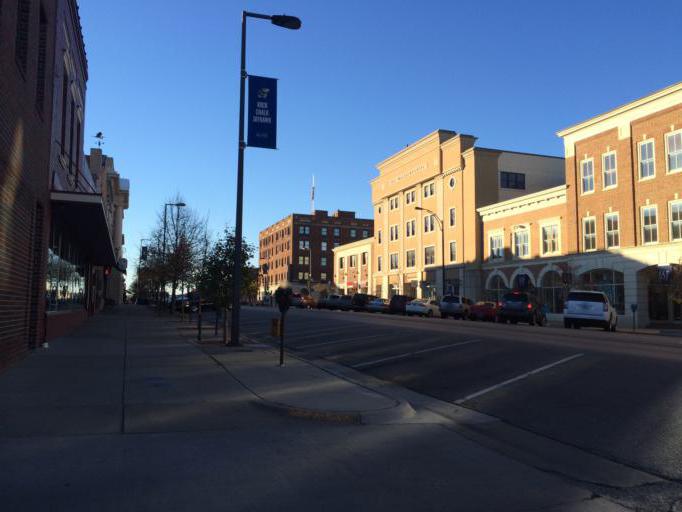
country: US
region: Kansas
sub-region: Douglas County
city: Lawrence
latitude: 38.9721
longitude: -95.2358
